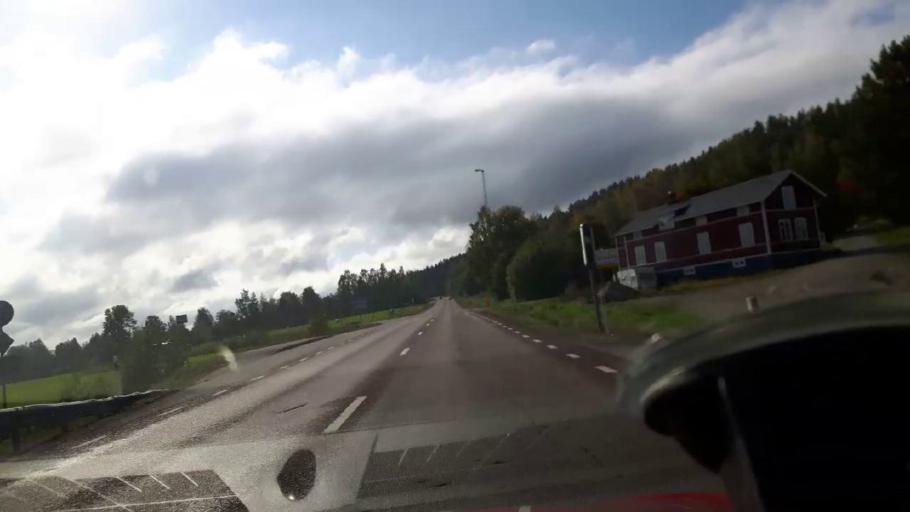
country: SE
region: Gaevleborg
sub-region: Ljusdals Kommun
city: Jaervsoe
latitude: 61.7482
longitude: 16.1597
